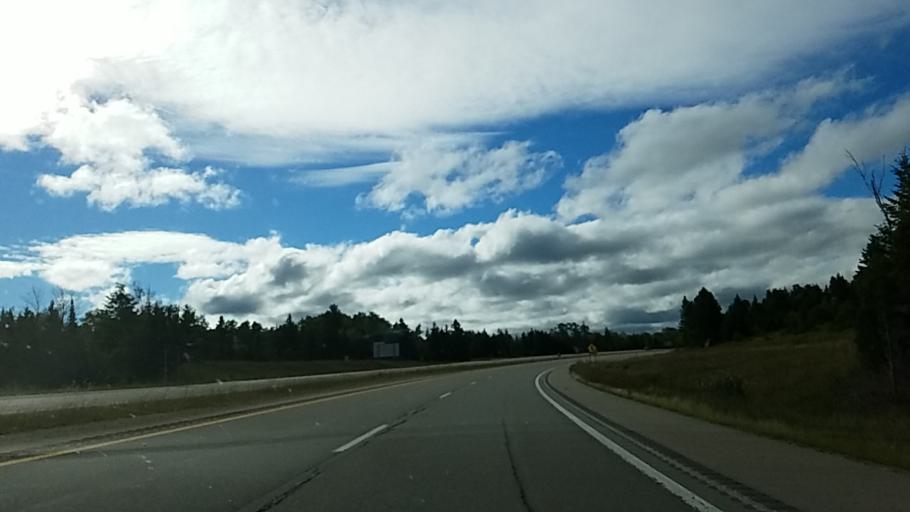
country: US
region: Michigan
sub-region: Mackinac County
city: Saint Ignace
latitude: 45.7617
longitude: -84.7308
